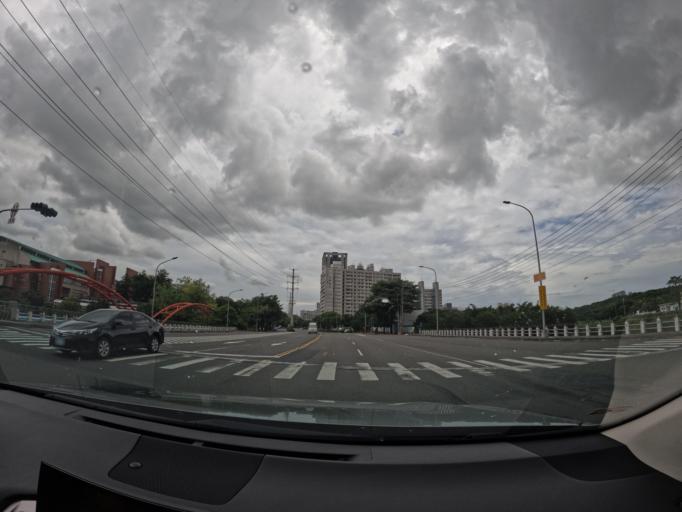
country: TW
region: Taiwan
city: Fengshan
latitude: 22.7298
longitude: 120.3144
